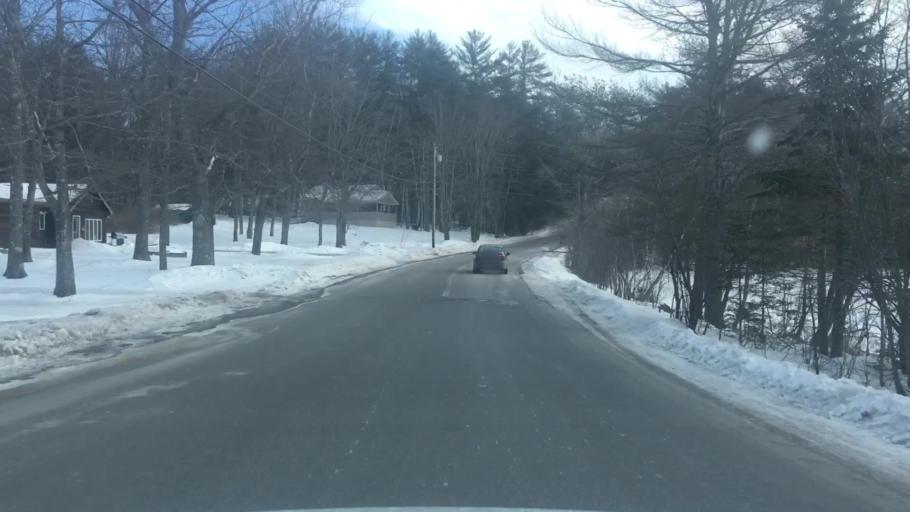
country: US
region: Maine
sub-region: Hancock County
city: Orland
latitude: 44.6300
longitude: -68.7024
